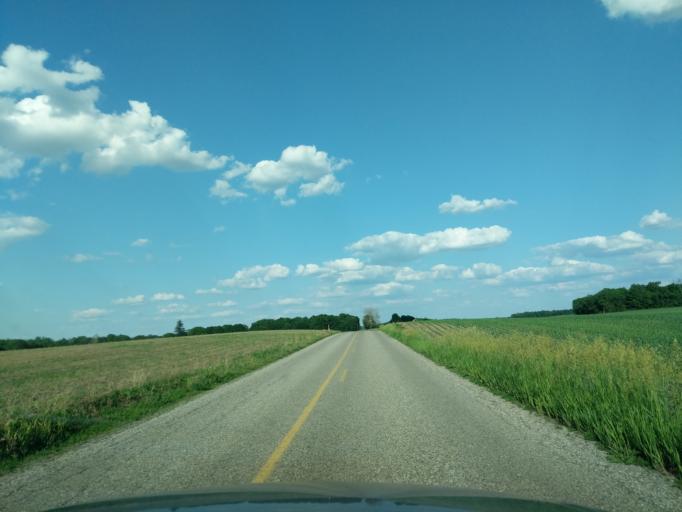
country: US
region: Indiana
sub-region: Kosciusko County
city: North Webster
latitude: 41.3024
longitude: -85.6303
